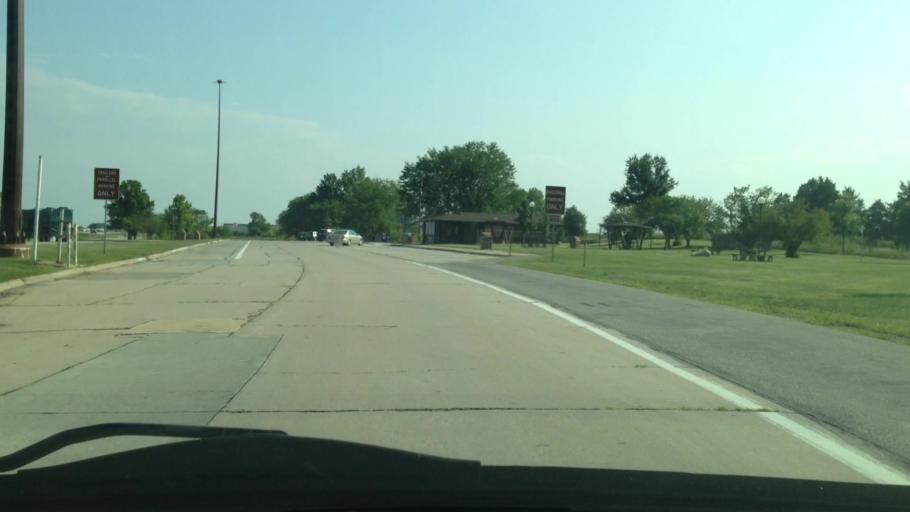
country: US
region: Iowa
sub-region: Linn County
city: Ely
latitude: 41.8681
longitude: -91.6707
